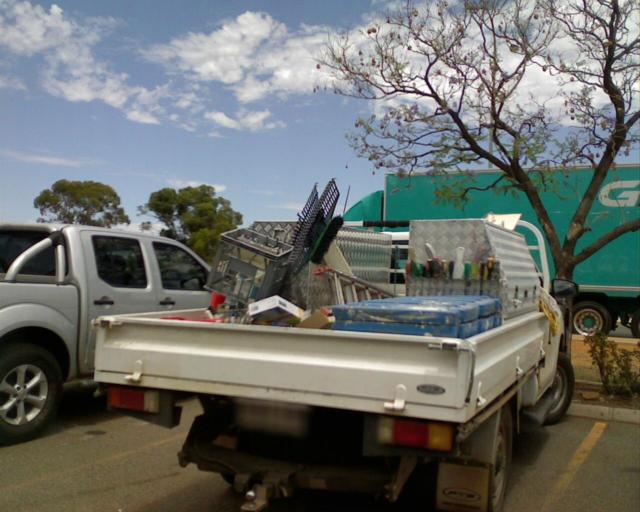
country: AU
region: Western Australia
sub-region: Kalgoorlie/Boulder
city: Boulder
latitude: -30.7755
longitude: 121.4605
